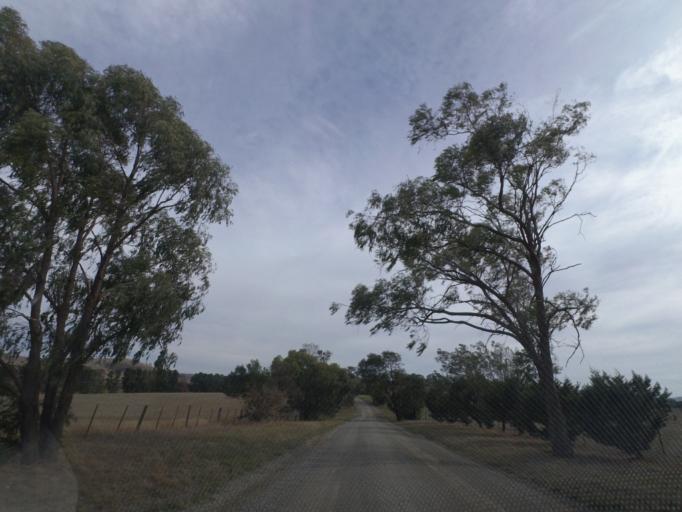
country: AU
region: Victoria
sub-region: Yarra Ranges
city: Yarra Glen
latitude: -37.6266
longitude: 145.4227
